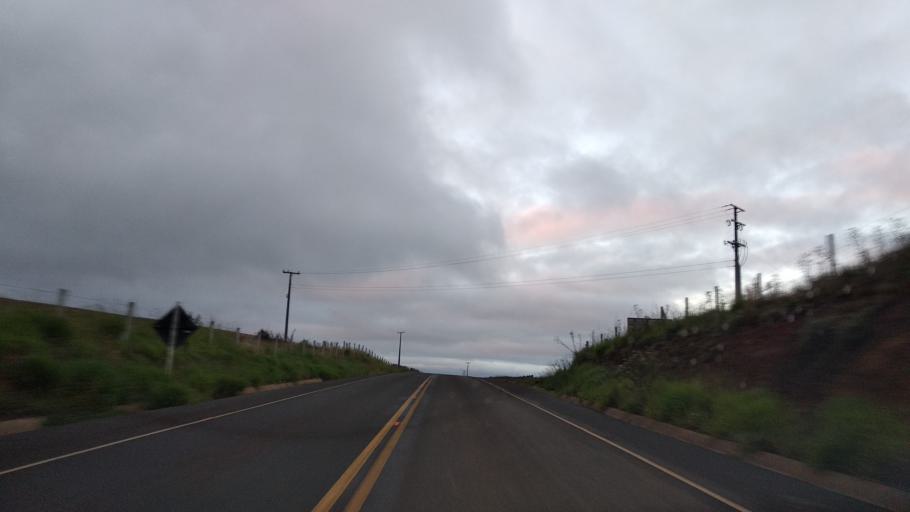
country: BR
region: Santa Catarina
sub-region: Campos Novos
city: Campos Novos
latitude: -27.3698
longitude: -51.2037
